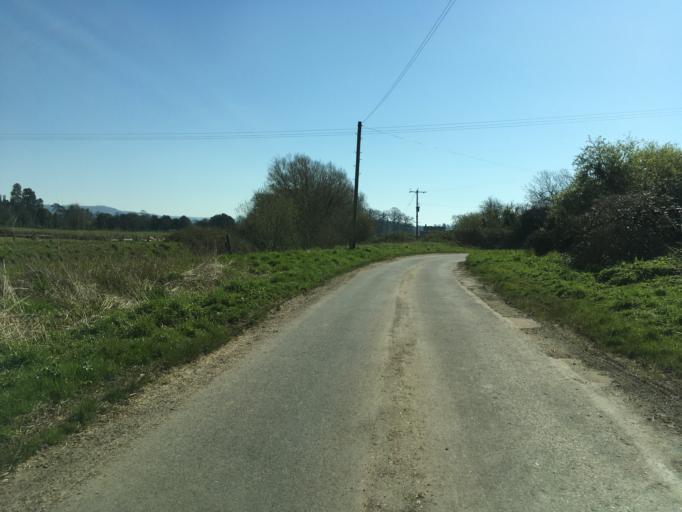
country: GB
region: England
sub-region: Gloucestershire
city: Berkeley
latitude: 51.6887
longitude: -2.4665
